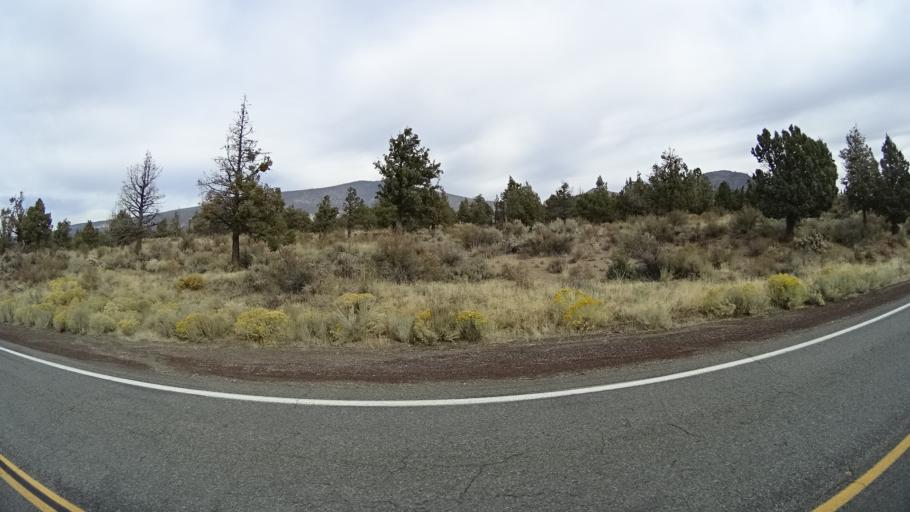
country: US
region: California
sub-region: Siskiyou County
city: Weed
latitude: 41.5689
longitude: -122.2685
